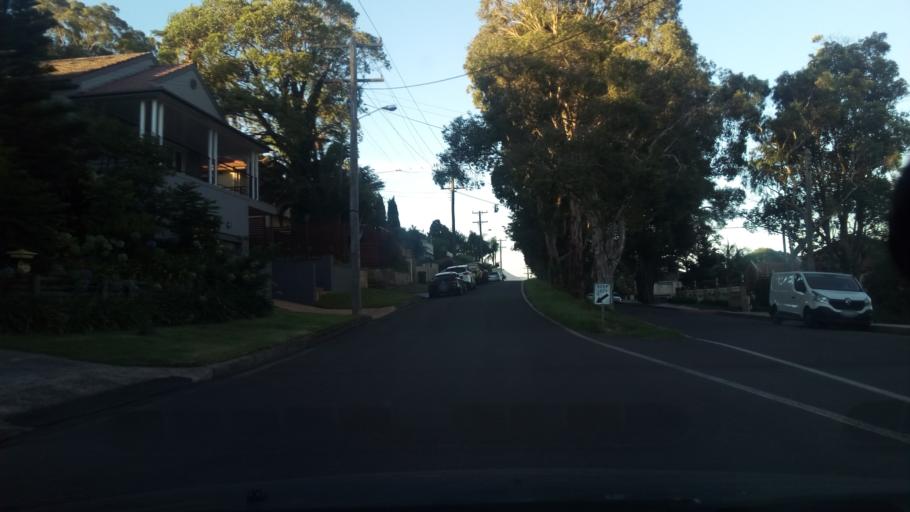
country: AU
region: New South Wales
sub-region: Wollongong
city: Mangerton
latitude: -34.4293
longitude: 150.8731
